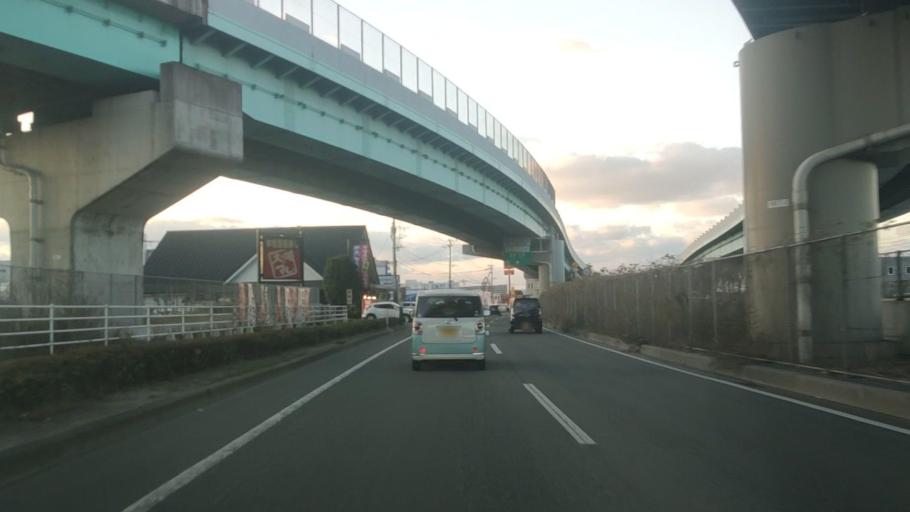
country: JP
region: Fukuoka
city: Onojo
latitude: 33.5655
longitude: 130.4620
